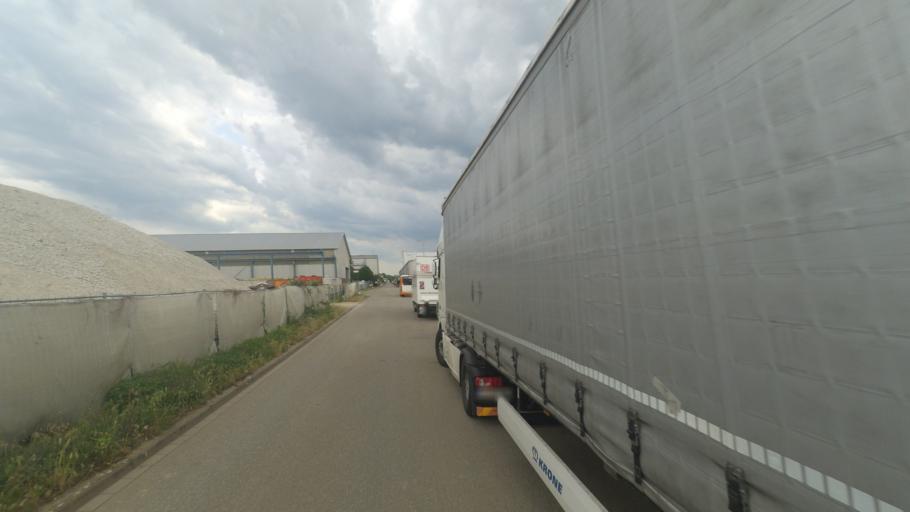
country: DE
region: Rheinland-Pfalz
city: Altrip
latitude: 49.4294
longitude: 8.5134
